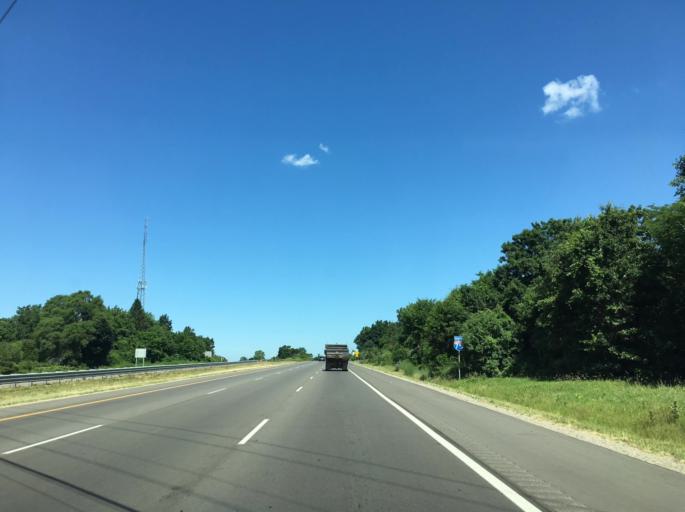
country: US
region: Michigan
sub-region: Oakland County
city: Clarkston
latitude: 42.7406
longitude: -83.3868
